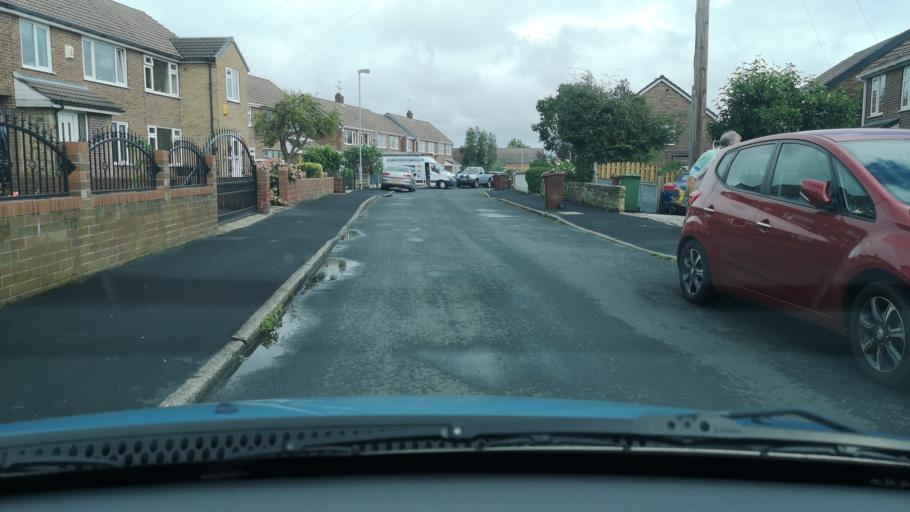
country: GB
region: England
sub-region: City and Borough of Wakefield
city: Low Ackworth
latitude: 53.6426
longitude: -1.3466
